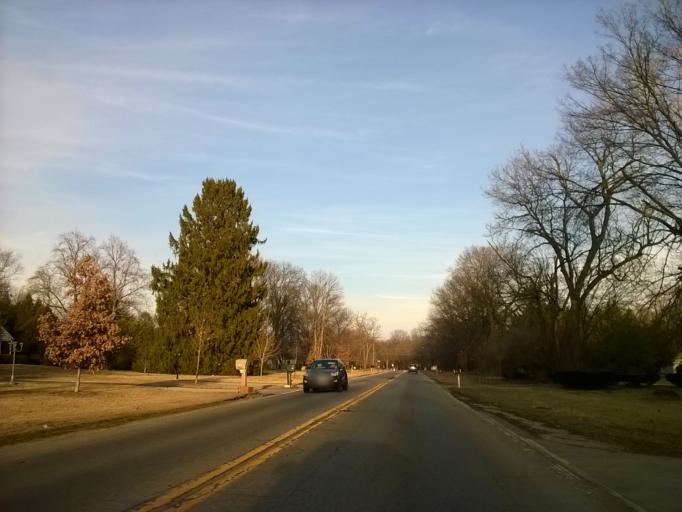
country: US
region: Indiana
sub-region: Marion County
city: Meridian Hills
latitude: 39.8576
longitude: -86.1814
